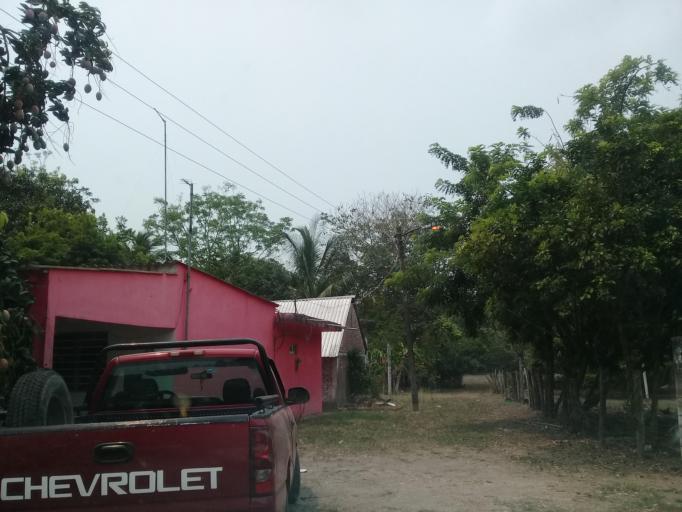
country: MX
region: Veracruz
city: Jamapa
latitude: 18.9513
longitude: -96.2042
